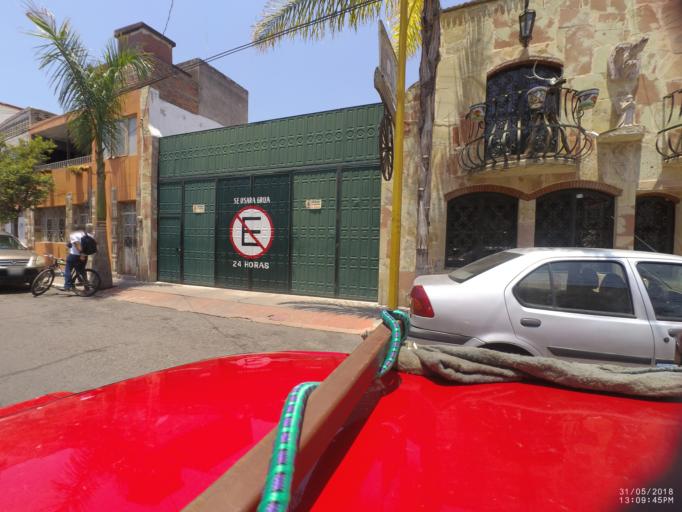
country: MX
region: Aguascalientes
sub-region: Aguascalientes
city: Aguascalientes
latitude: 21.8743
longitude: -102.2936
